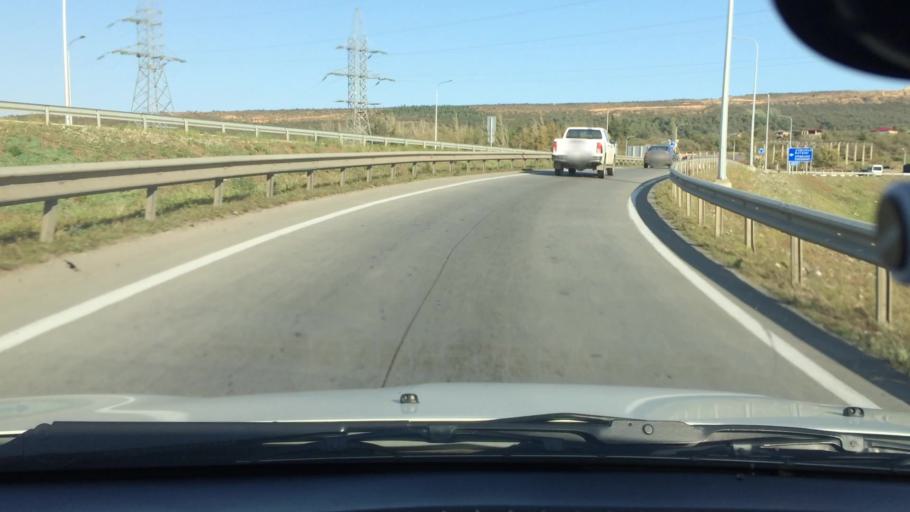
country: GE
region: Imereti
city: Kutaisi
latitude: 42.2119
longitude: 42.8198
